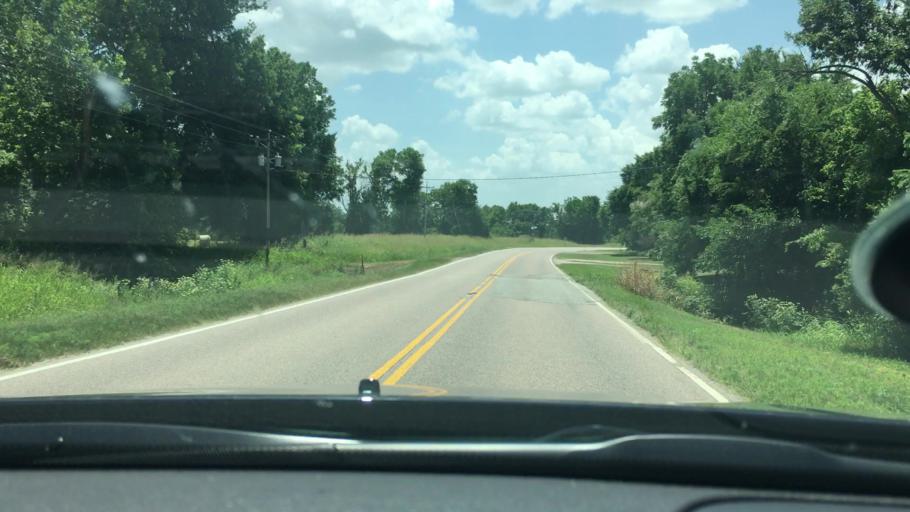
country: US
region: Oklahoma
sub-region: Johnston County
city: Tishomingo
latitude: 34.4863
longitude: -96.6267
